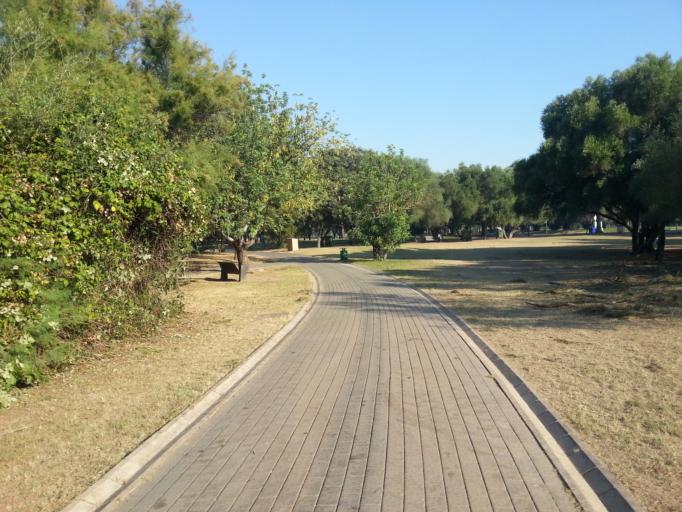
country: ES
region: Andalusia
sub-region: Provincia de Sevilla
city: Camas
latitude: 37.4198
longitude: -5.9955
